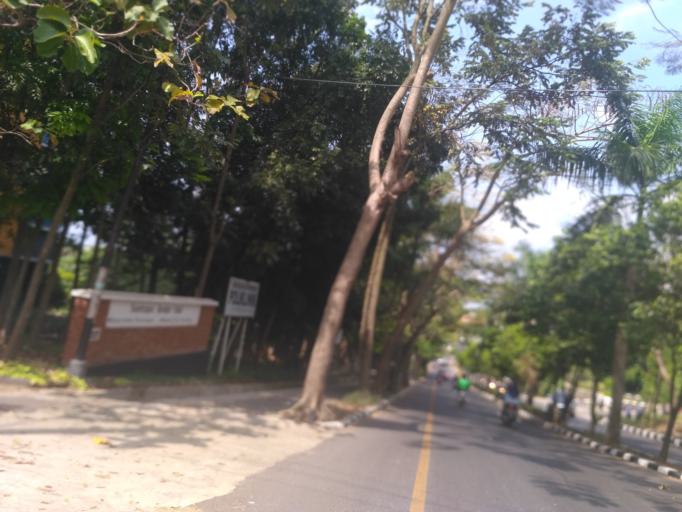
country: ID
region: Central Java
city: Semarang
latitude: -7.0544
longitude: 110.4396
